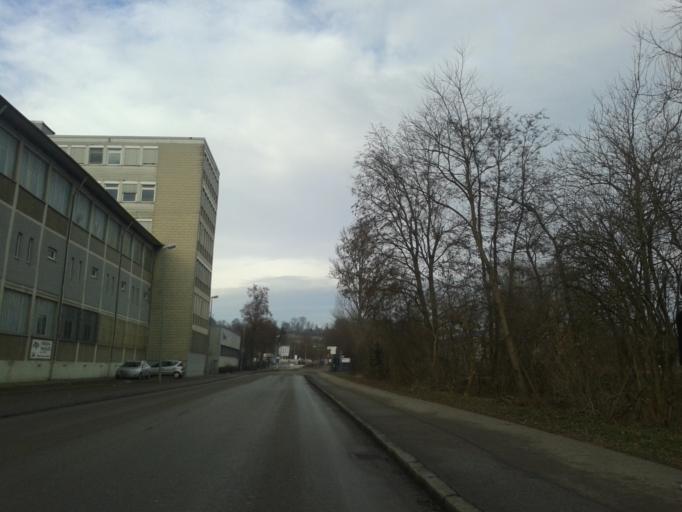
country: DE
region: Baden-Wuerttemberg
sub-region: Tuebingen Region
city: Ulm
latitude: 48.3692
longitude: 9.9536
